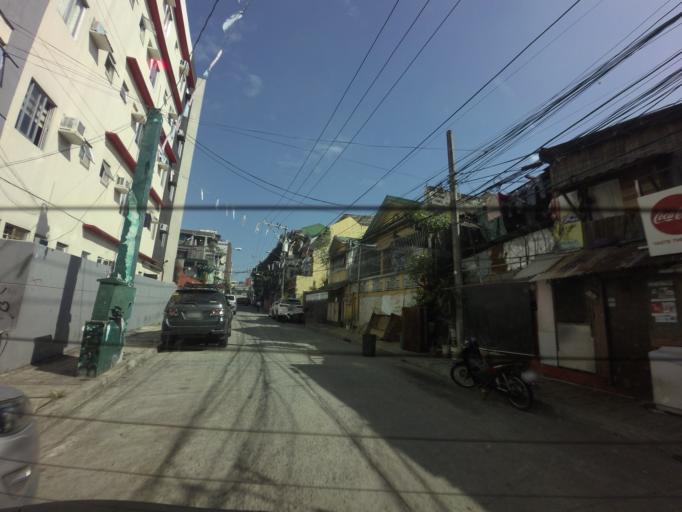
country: PH
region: Metro Manila
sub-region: Makati City
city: Makati City
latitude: 14.5594
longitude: 121.0454
